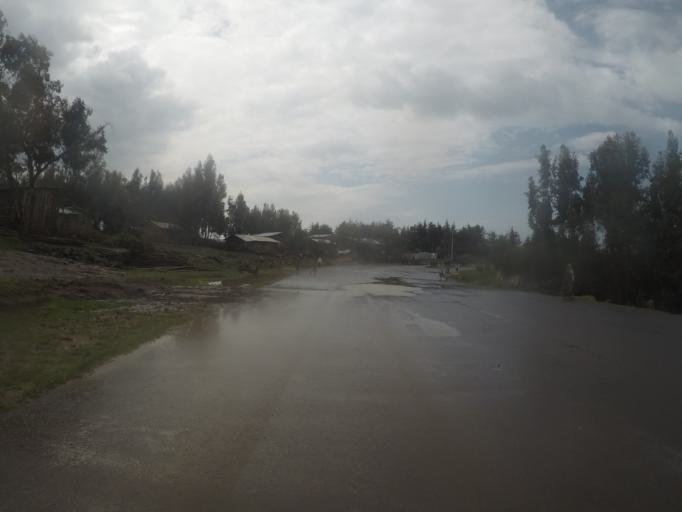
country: ET
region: Amhara
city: Debark'
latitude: 13.1402
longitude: 37.8939
